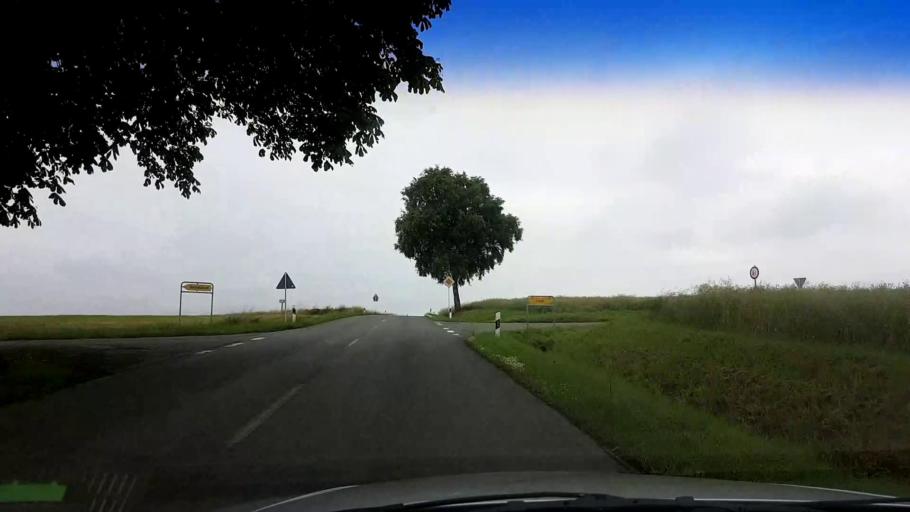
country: DE
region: Bavaria
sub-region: Upper Franconia
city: Kasendorf
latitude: 50.0706
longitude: 11.3366
